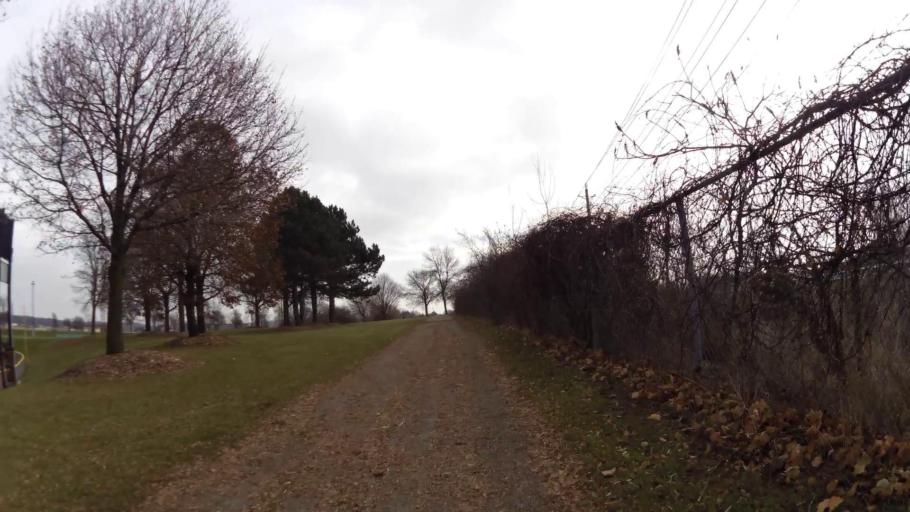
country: CA
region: Ontario
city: Kitchener
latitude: 43.3995
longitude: -80.4546
